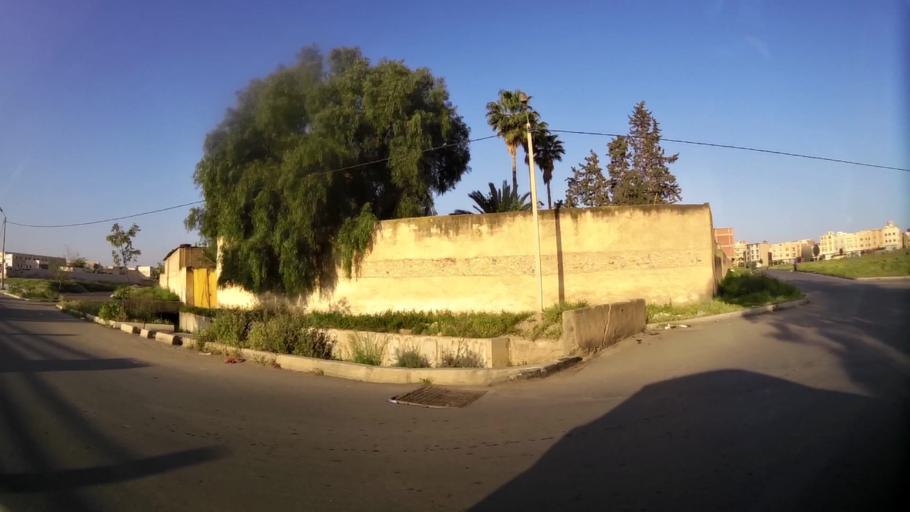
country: MA
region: Oriental
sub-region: Oujda-Angad
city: Oujda
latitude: 34.6732
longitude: -1.9368
